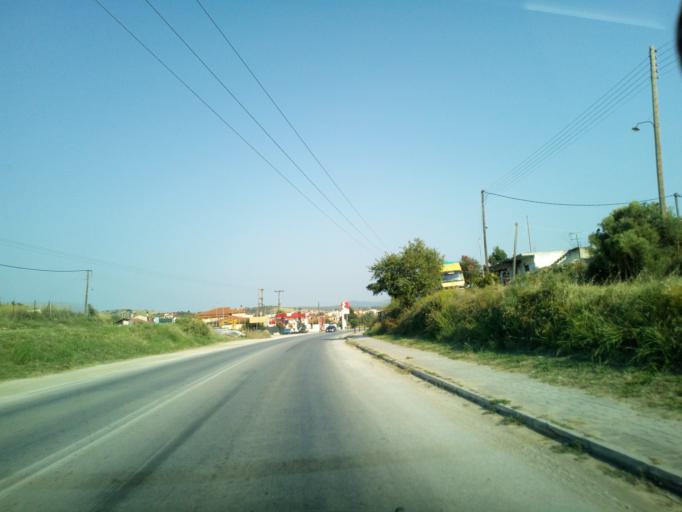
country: GR
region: Central Macedonia
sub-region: Nomos Chalkidikis
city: Nikiti
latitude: 40.2262
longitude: 23.6631
